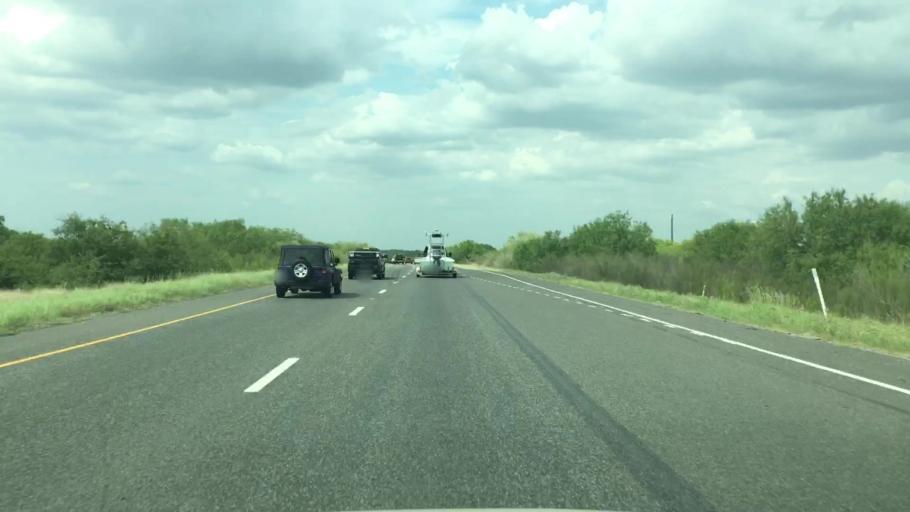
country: US
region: Texas
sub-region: Atascosa County
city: Pleasanton
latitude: 28.9207
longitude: -98.4347
